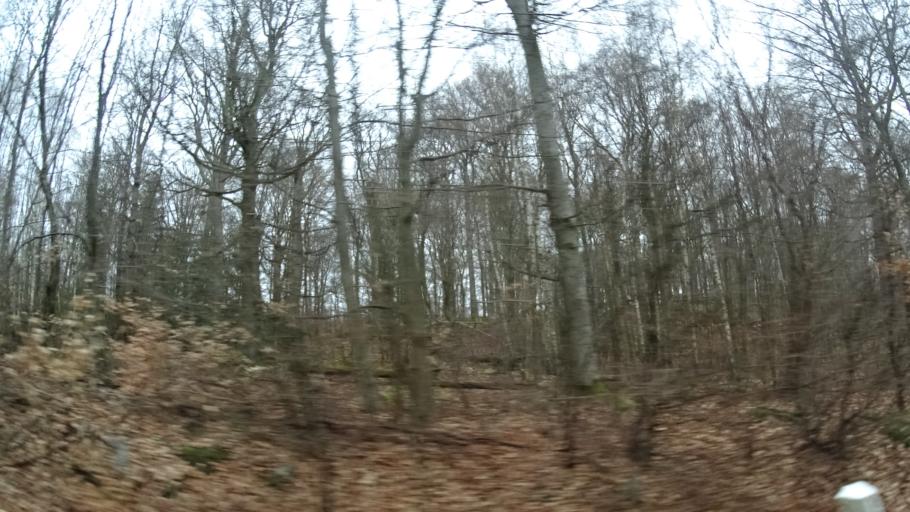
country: DE
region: Rheinland-Pfalz
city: Ippenschied
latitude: 49.8944
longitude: 7.6196
